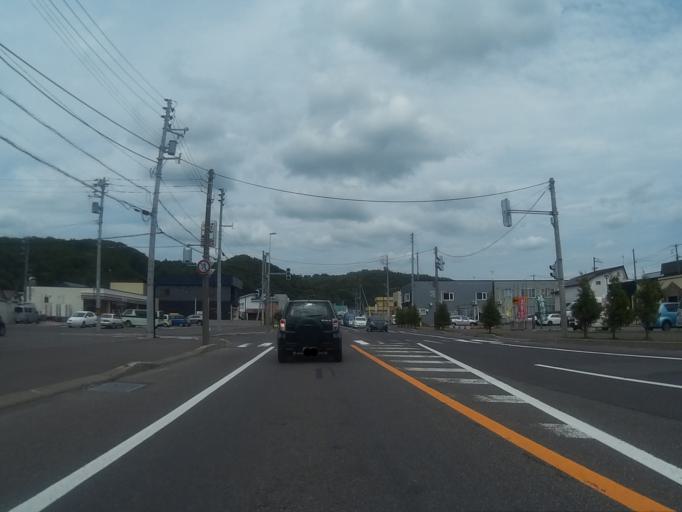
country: JP
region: Hokkaido
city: Niseko Town
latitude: 42.7945
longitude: 140.9370
